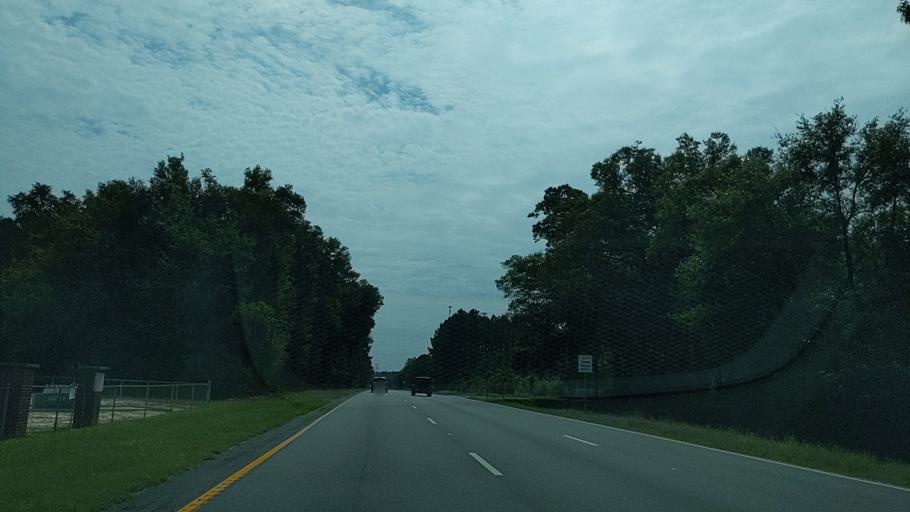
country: US
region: Georgia
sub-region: Effingham County
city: Rincon
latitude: 32.2498
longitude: -81.2118
